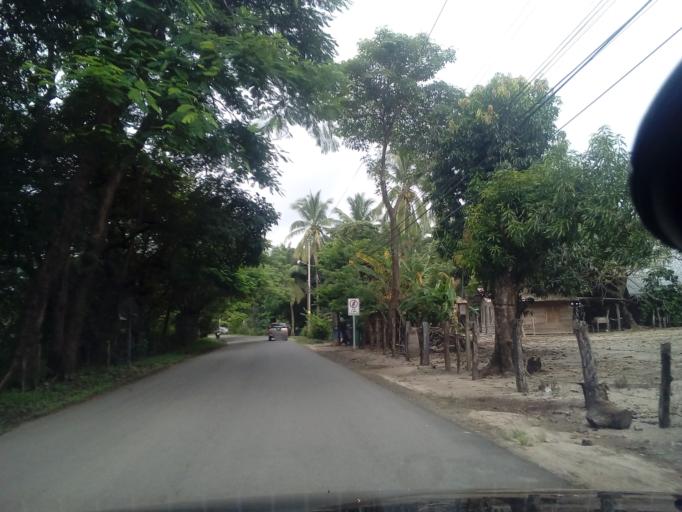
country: CR
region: Guanacaste
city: Samara
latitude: 9.9105
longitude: -85.6421
